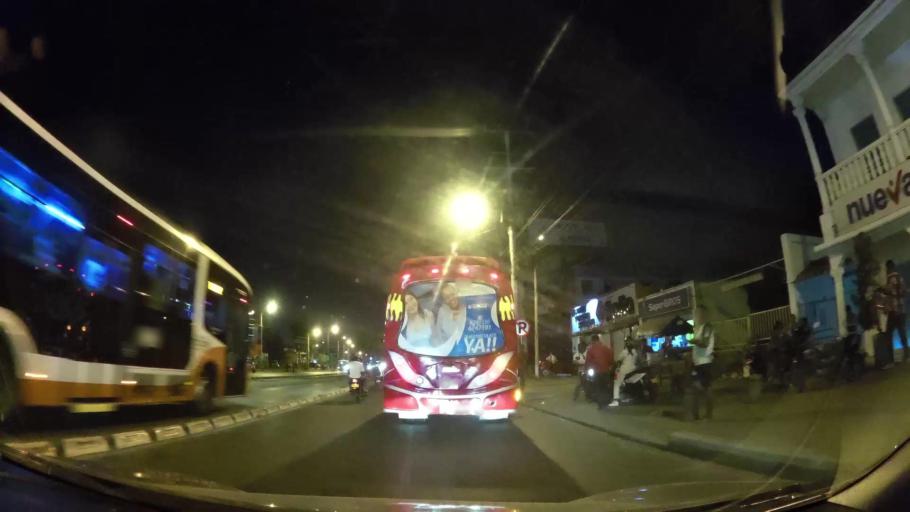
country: CO
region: Bolivar
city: Cartagena
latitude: 10.4105
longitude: -75.5188
